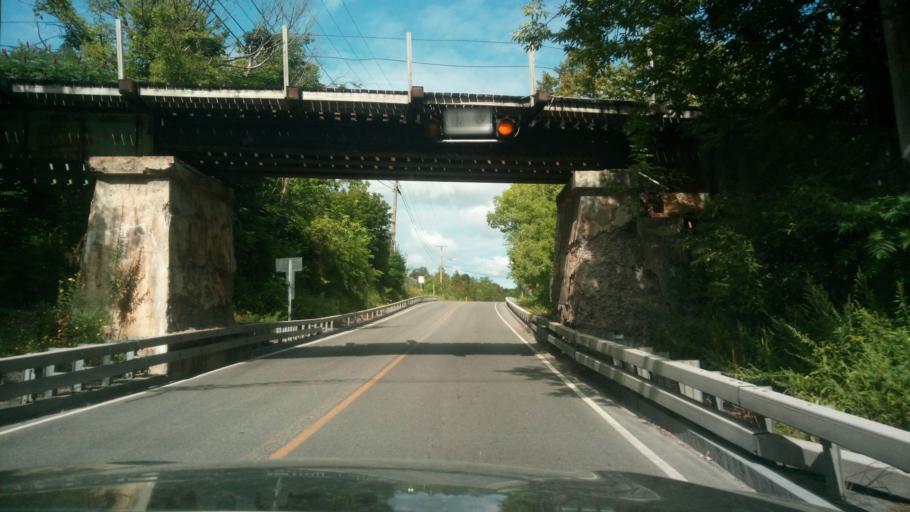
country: US
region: New York
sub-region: Onondaga County
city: East Syracuse
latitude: 43.0014
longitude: -76.0748
